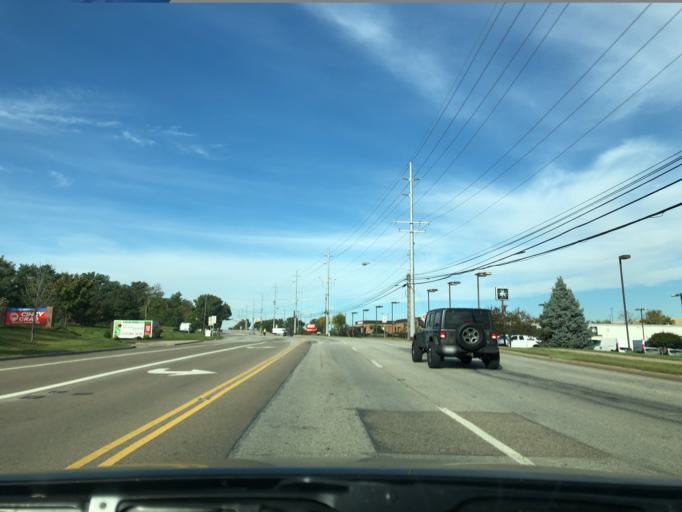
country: US
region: Ohio
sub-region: Hamilton County
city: Glendale
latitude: 39.2860
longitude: -84.4488
